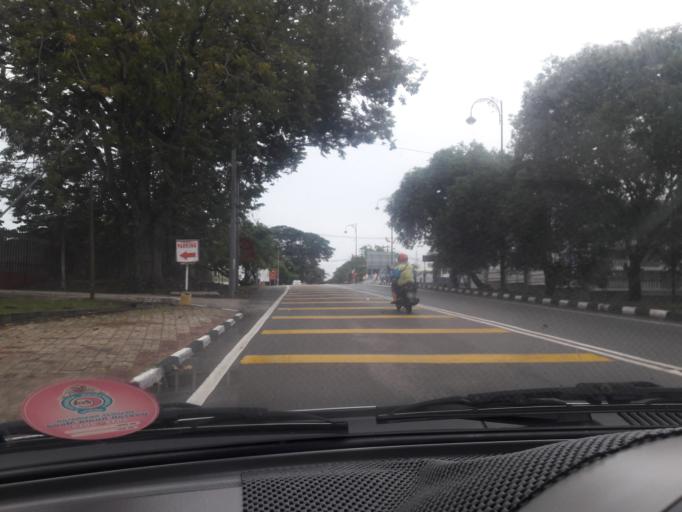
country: MY
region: Kedah
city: Sungai Petani
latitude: 5.6475
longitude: 100.4884
